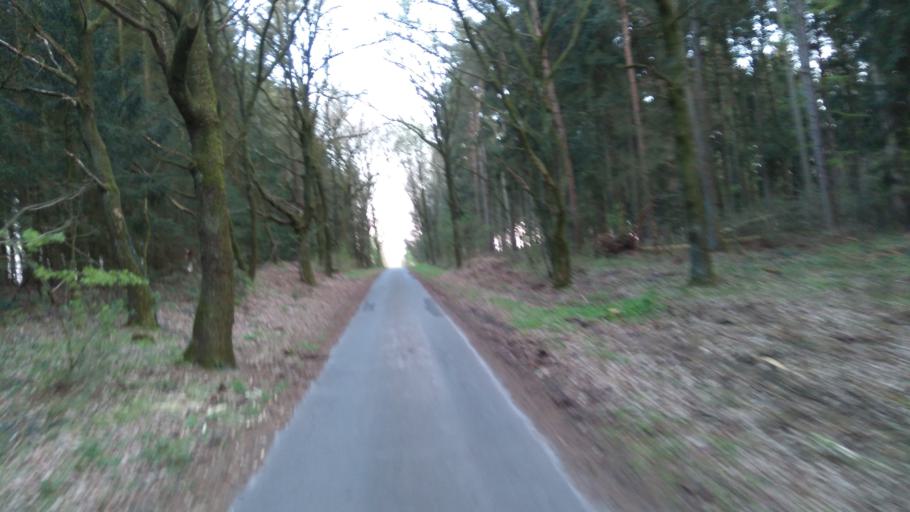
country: DE
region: Lower Saxony
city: Bargstedt
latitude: 53.4546
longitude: 9.4653
